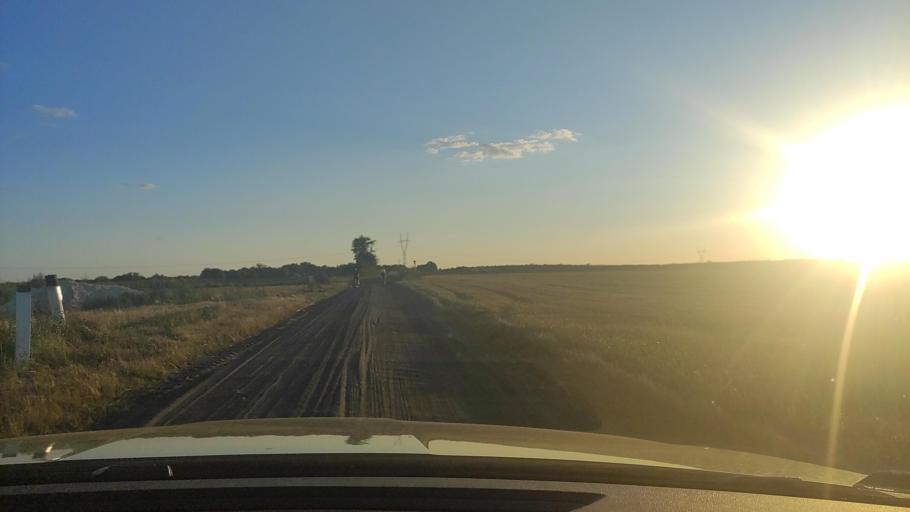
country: PL
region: Greater Poland Voivodeship
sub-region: Powiat poznanski
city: Kobylnica
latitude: 52.4552
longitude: 17.1431
